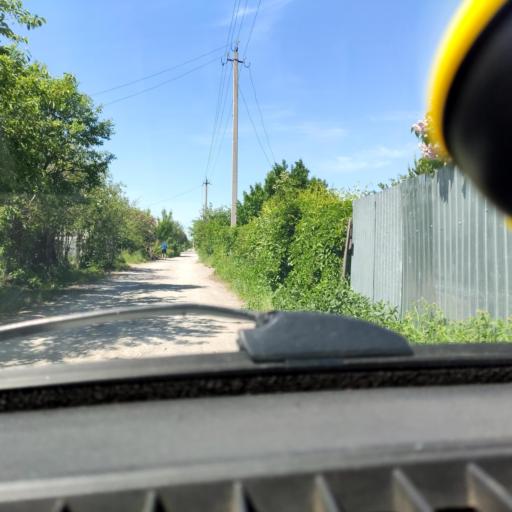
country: RU
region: Samara
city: Povolzhskiy
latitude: 53.6138
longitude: 49.6222
